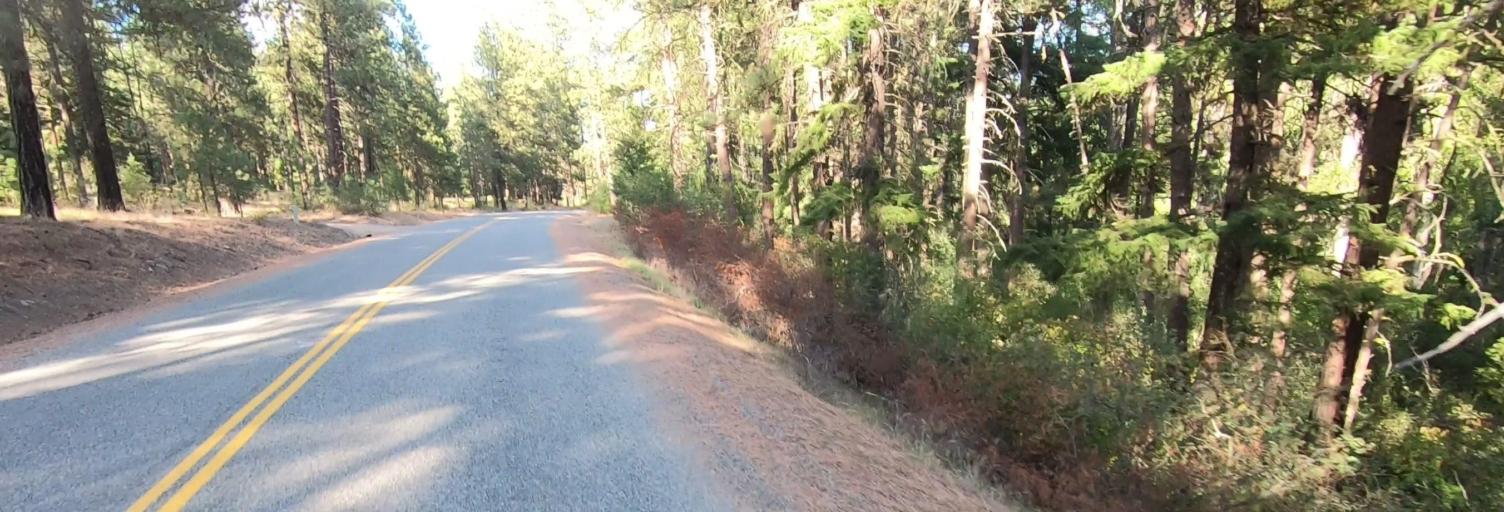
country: US
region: Washington
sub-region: Kittitas County
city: Cle Elum
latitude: 47.2441
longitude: -120.6938
